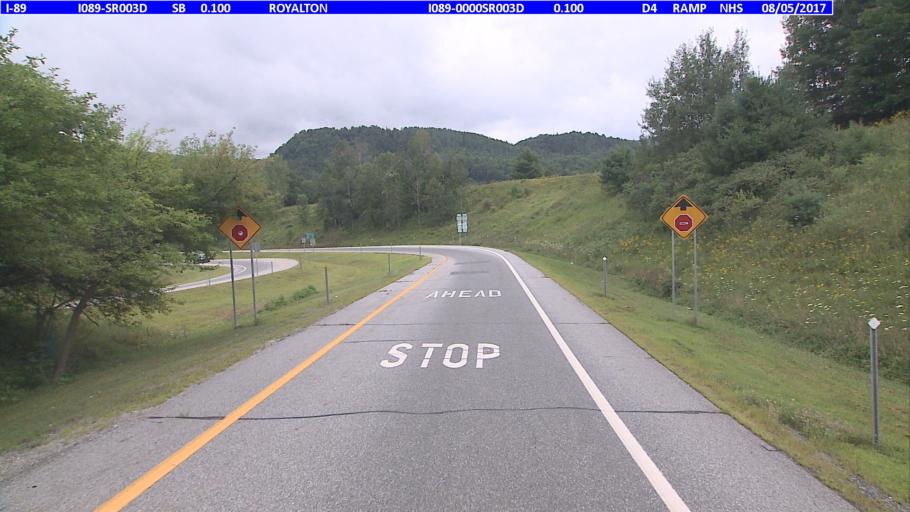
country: US
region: Vermont
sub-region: Orange County
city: Randolph
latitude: 43.8279
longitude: -72.5823
